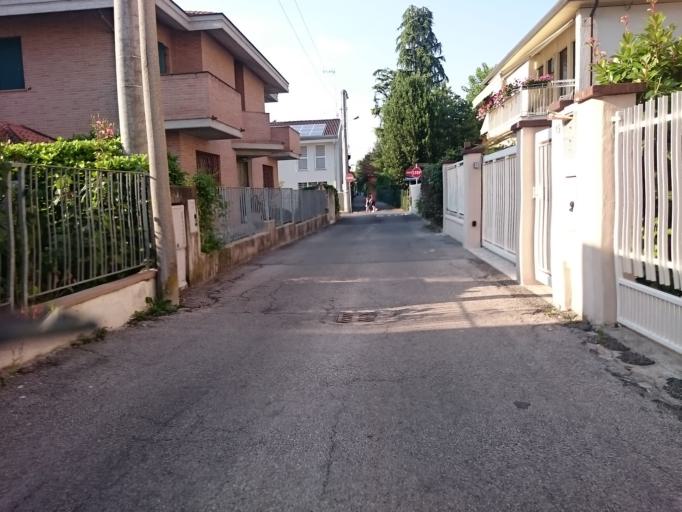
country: IT
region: Veneto
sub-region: Provincia di Padova
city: Padova
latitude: 45.3928
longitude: 11.8885
